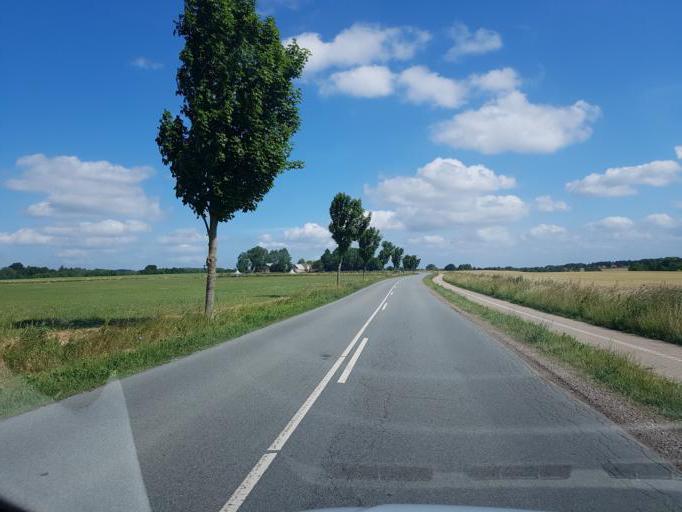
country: DK
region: Zealand
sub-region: Lejre Kommune
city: Lejre
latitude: 55.5852
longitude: 11.9690
